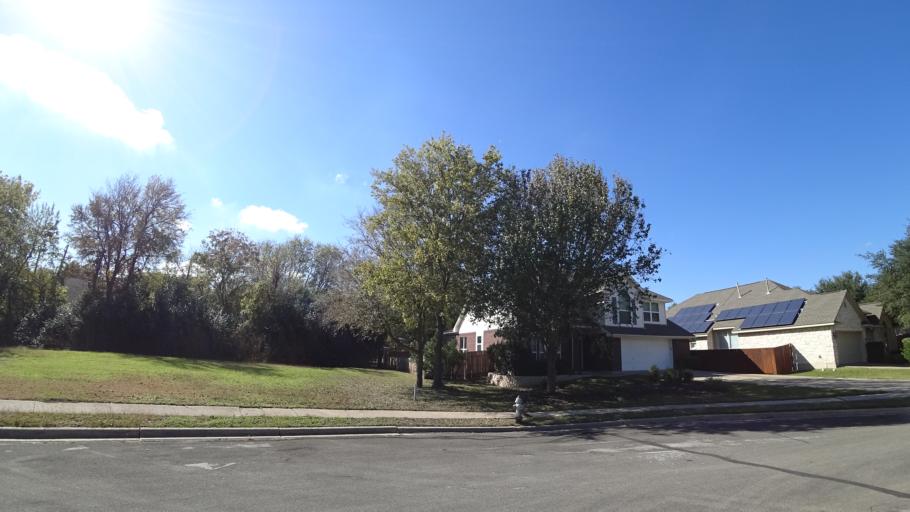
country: US
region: Texas
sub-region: Travis County
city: Wells Branch
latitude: 30.4248
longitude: -97.6852
